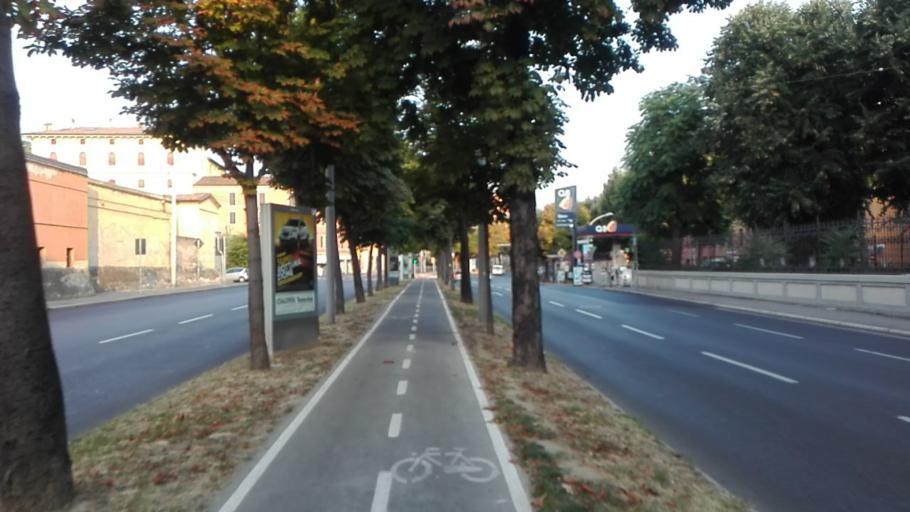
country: IT
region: Emilia-Romagna
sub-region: Provincia di Bologna
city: Bologna
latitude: 44.4863
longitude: 11.3410
